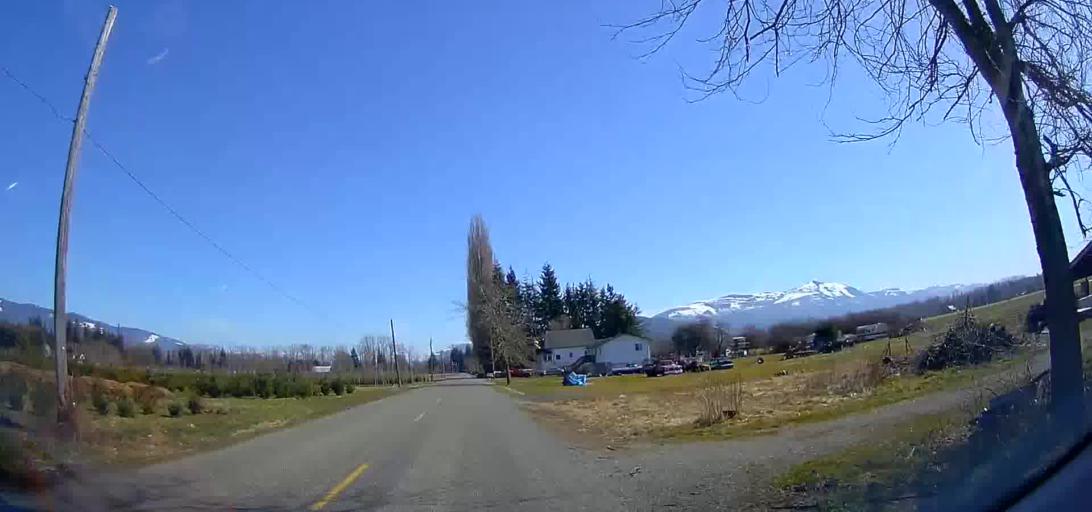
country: US
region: Washington
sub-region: Skagit County
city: Burlington
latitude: 48.4893
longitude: -122.2838
